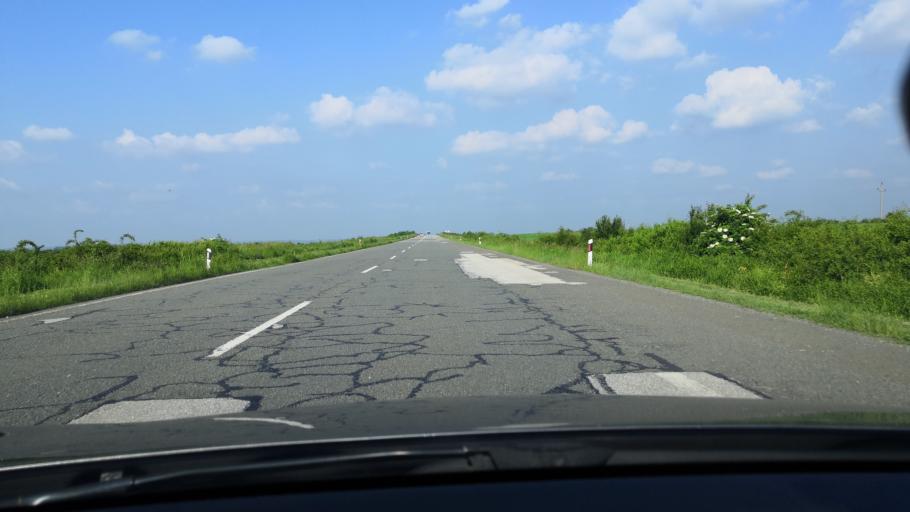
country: RS
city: Beska
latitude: 45.0923
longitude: 20.0659
